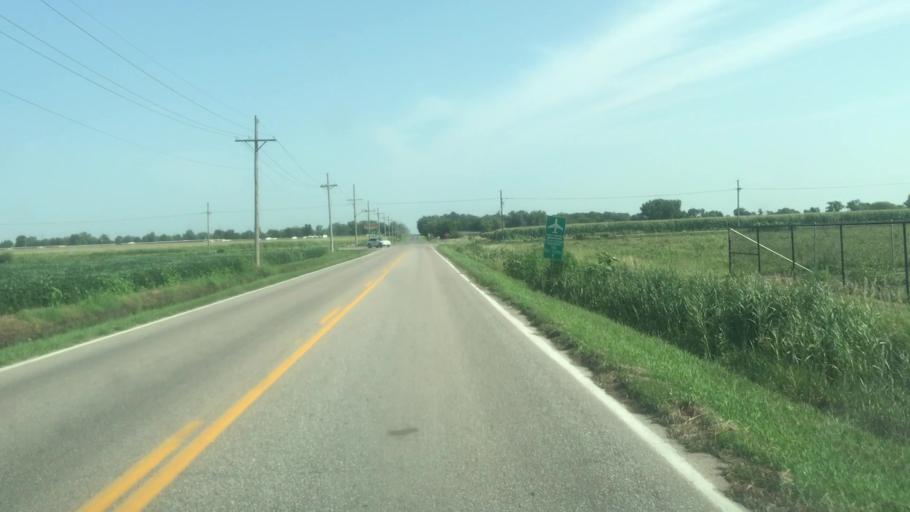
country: US
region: Nebraska
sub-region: Hall County
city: Grand Island
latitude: 40.9438
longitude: -98.3015
